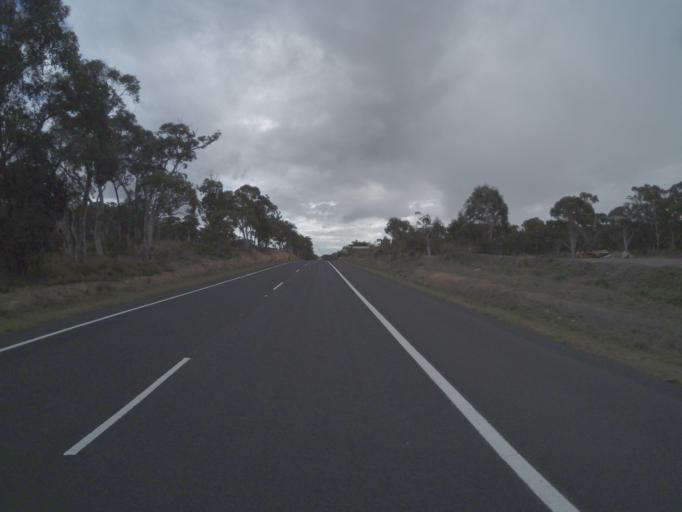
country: AU
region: New South Wales
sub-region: Goulburn Mulwaree
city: Goulburn
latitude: -34.7434
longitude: 149.8949
